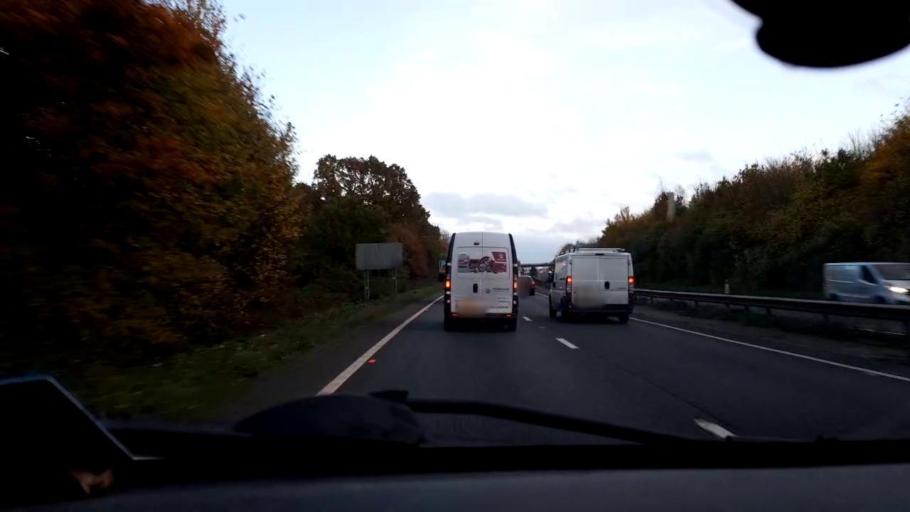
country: GB
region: England
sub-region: Norfolk
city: Bowthorpe
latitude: 52.6203
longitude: 1.2062
